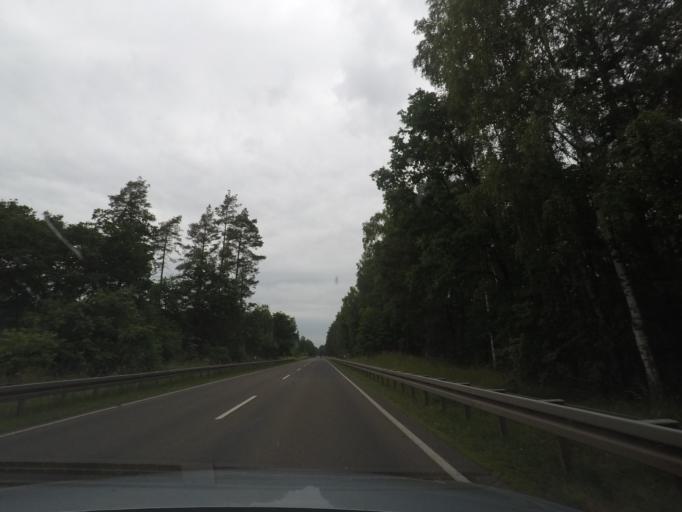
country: DE
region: Saxony-Anhalt
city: Colbitz
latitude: 52.3450
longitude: 11.5752
